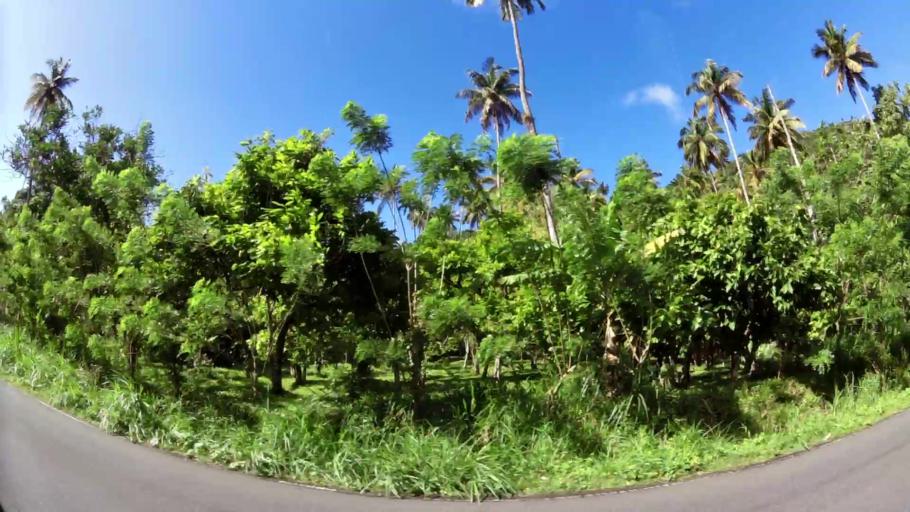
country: LC
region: Soufriere
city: Soufriere
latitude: 13.8232
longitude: -61.0485
